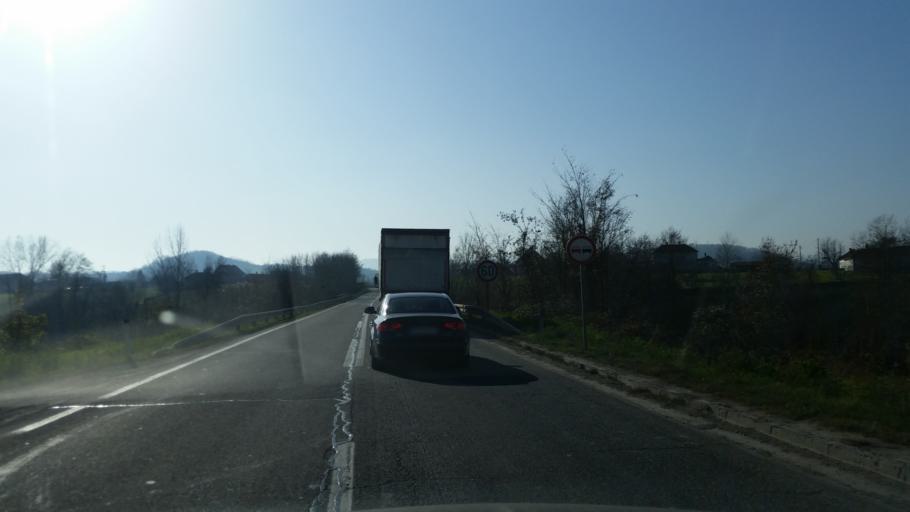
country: RS
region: Central Serbia
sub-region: Kolubarski Okrug
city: Ljig
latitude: 44.2535
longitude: 20.2859
